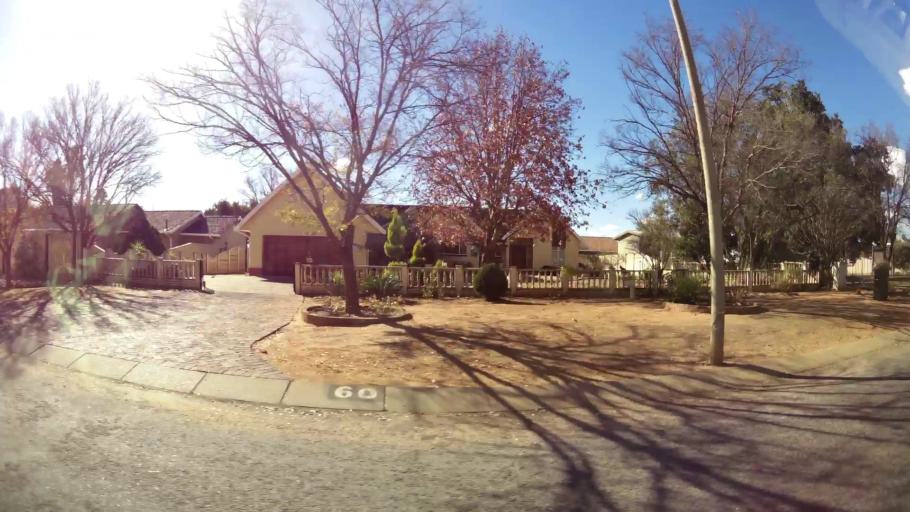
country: ZA
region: North-West
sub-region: Dr Kenneth Kaunda District Municipality
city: Klerksdorp
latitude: -26.8242
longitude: 26.6546
